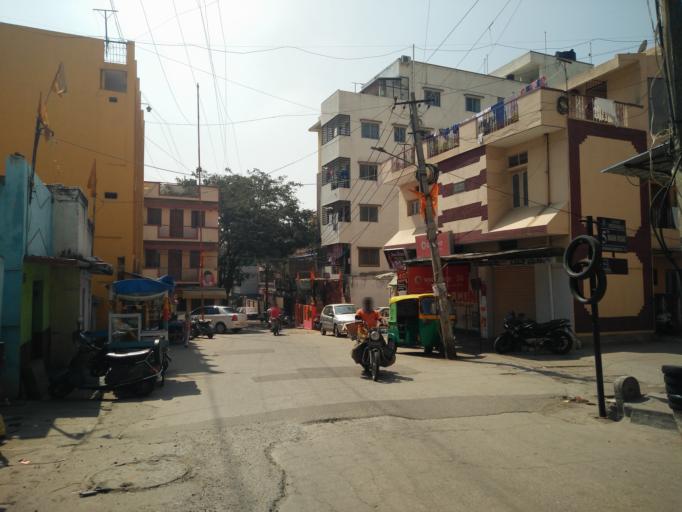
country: IN
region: Karnataka
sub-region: Bangalore Urban
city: Bangalore
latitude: 12.9693
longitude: 77.5420
